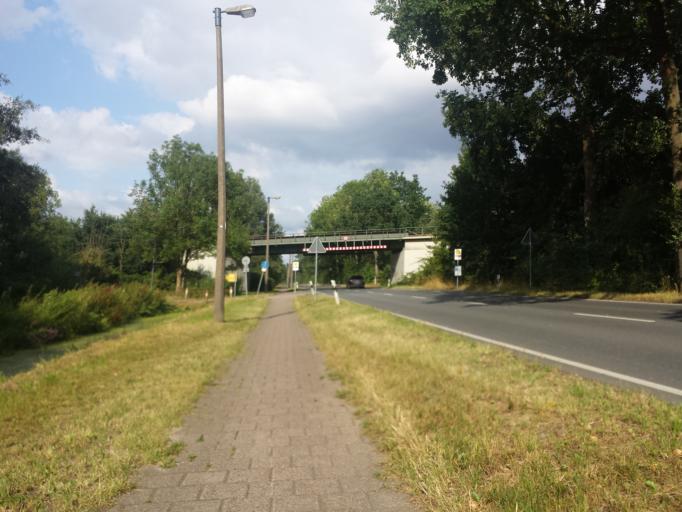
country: DE
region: Lower Saxony
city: Stuhr
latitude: 53.0793
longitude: 8.7412
